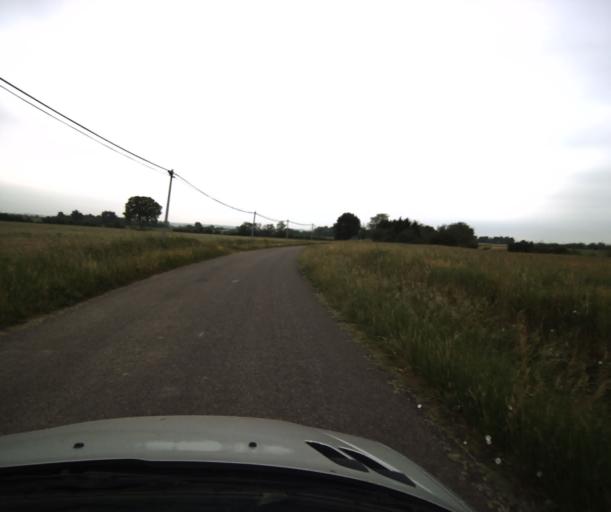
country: FR
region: Midi-Pyrenees
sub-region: Departement du Tarn-et-Garonne
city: Saint-Nicolas-de-la-Grave
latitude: 44.0576
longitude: 1.0045
